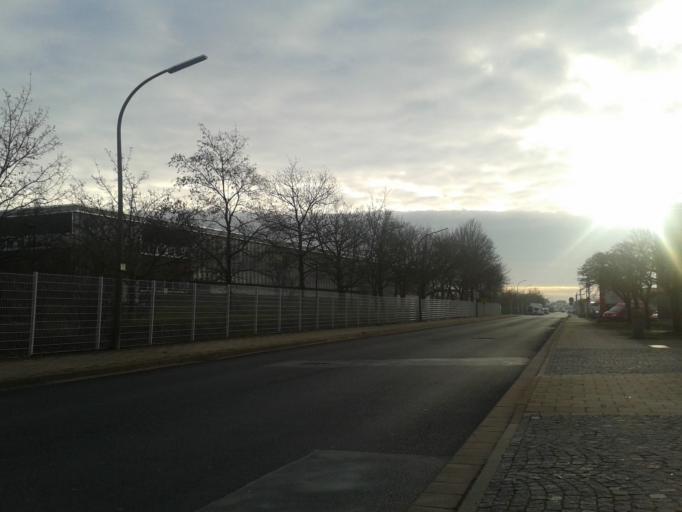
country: DE
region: Bavaria
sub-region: Upper Franconia
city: Hallstadt
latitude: 49.9137
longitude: 10.8748
